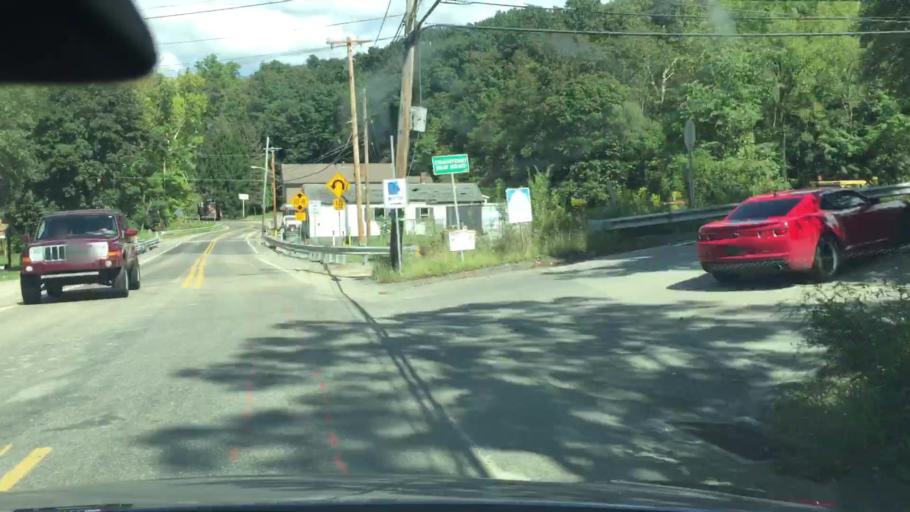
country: US
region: Pennsylvania
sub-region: Allegheny County
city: Russellton
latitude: 40.5891
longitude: -79.8276
